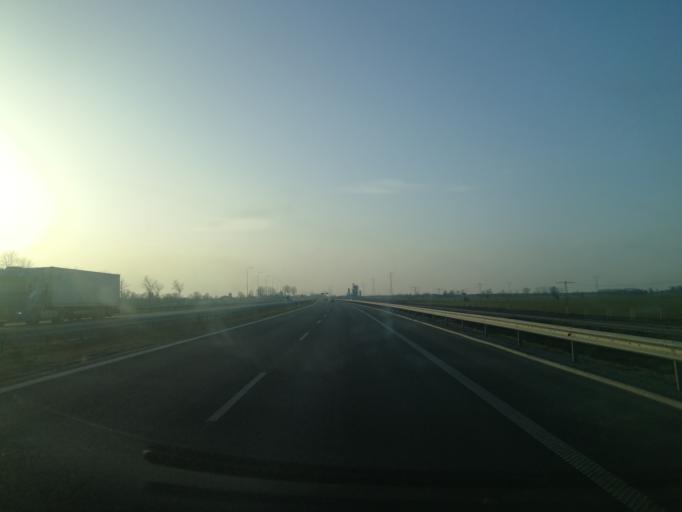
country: PL
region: Pomeranian Voivodeship
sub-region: Powiat nowodworski
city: Ostaszewo
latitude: 54.2535
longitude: 18.9732
